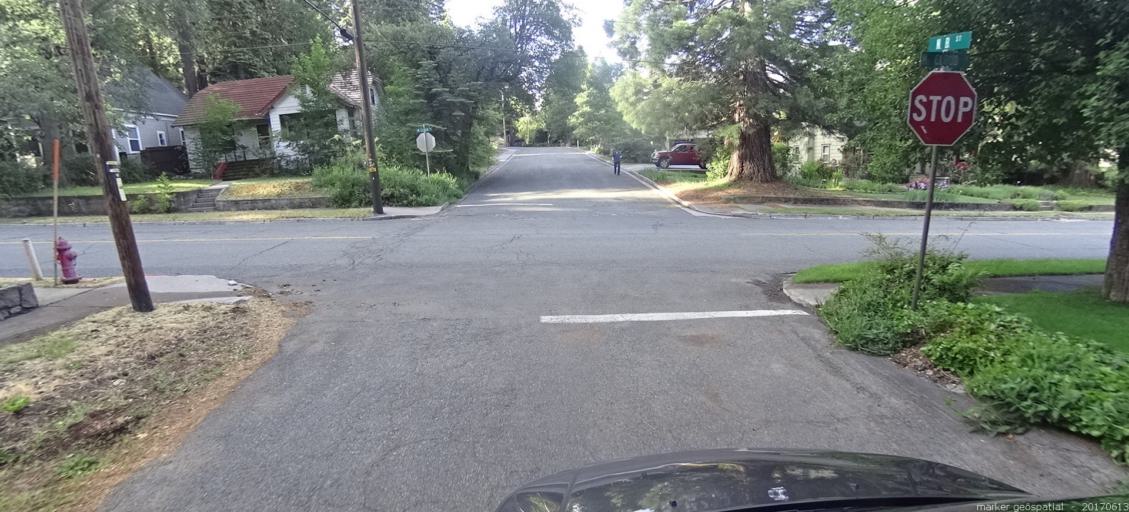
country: US
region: California
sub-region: Siskiyou County
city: Mount Shasta
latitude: 41.3124
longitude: -122.3084
